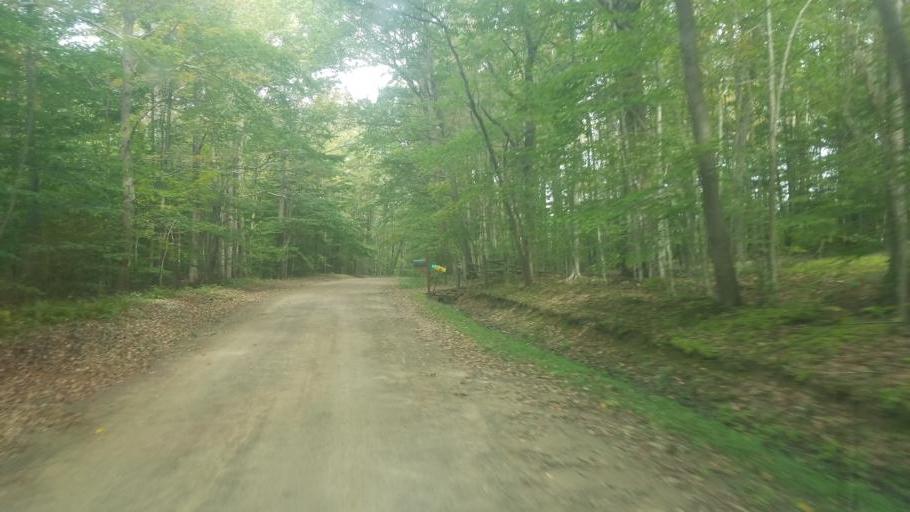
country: US
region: New York
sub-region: Allegany County
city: Cuba
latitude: 42.1414
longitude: -78.3018
